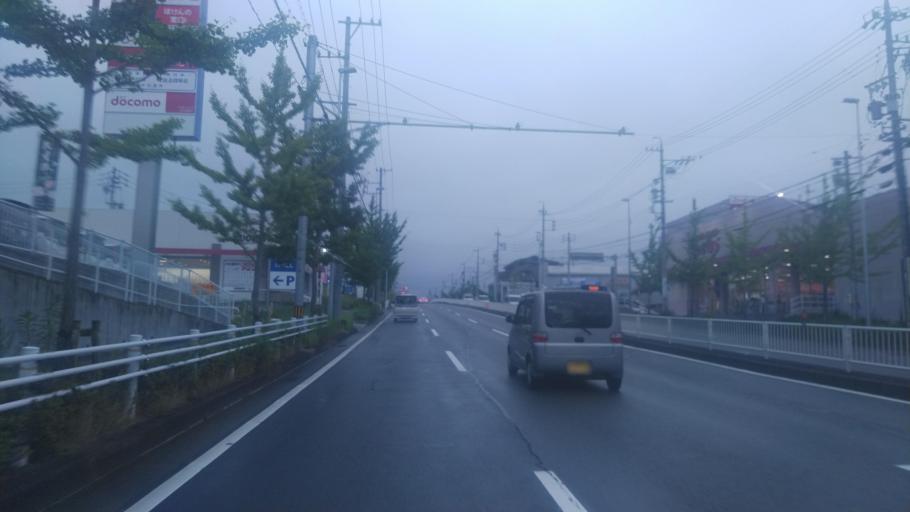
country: JP
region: Aichi
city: Kasugai
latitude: 35.2414
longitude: 137.0151
